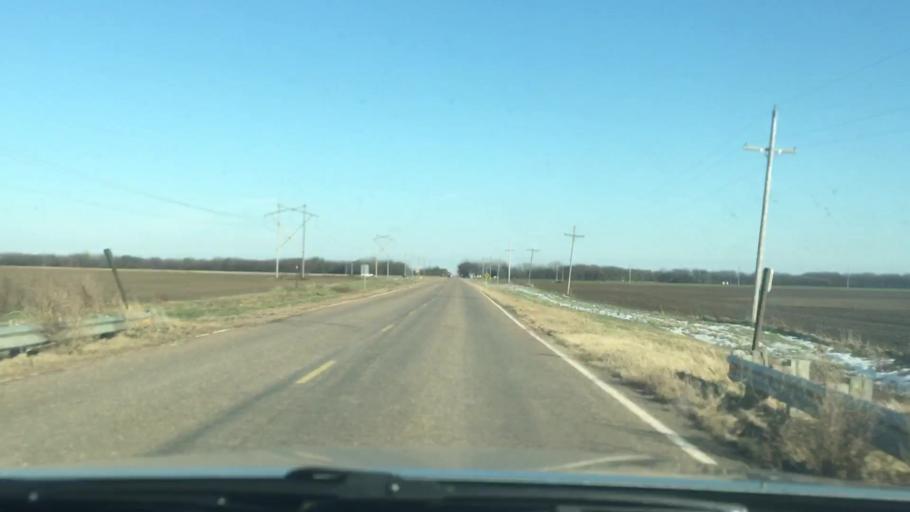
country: US
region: Kansas
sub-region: Rice County
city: Lyons
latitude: 38.2896
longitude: -98.1328
